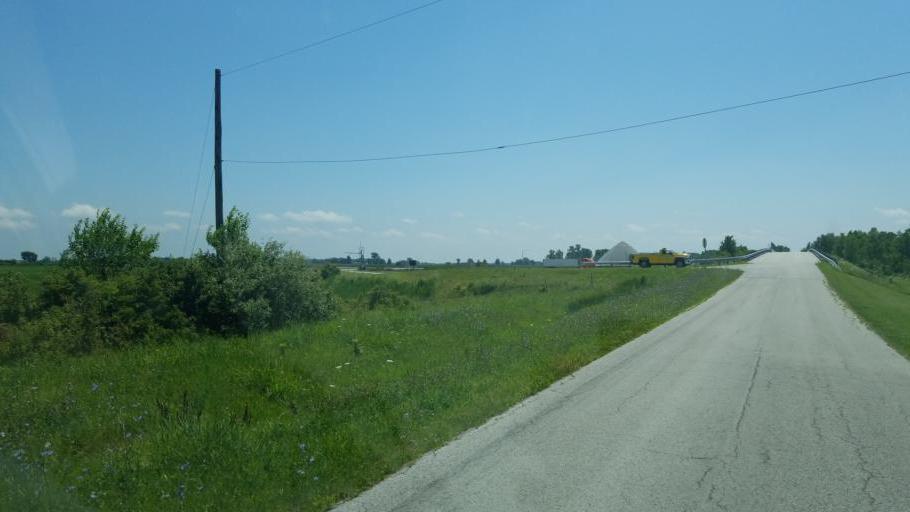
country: US
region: Ohio
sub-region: Sandusky County
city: Fremont
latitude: 41.3969
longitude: -83.0873
